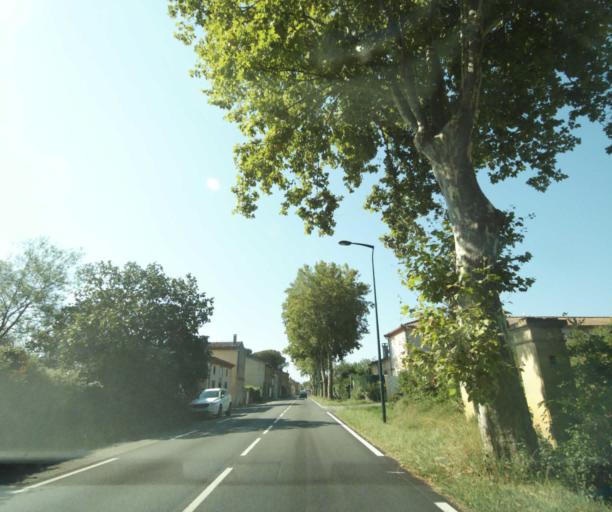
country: FR
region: Midi-Pyrenees
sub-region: Departement de la Haute-Garonne
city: Saint-Sulpice-sur-Leze
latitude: 43.3320
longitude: 1.3221
